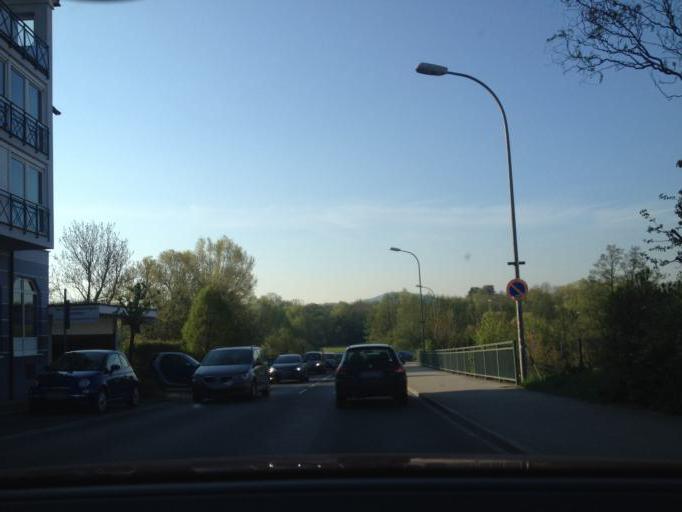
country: DE
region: Bavaria
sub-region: Regierungsbezirk Mittelfranken
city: Lauf an der Pegnitz
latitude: 49.5127
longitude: 11.2847
